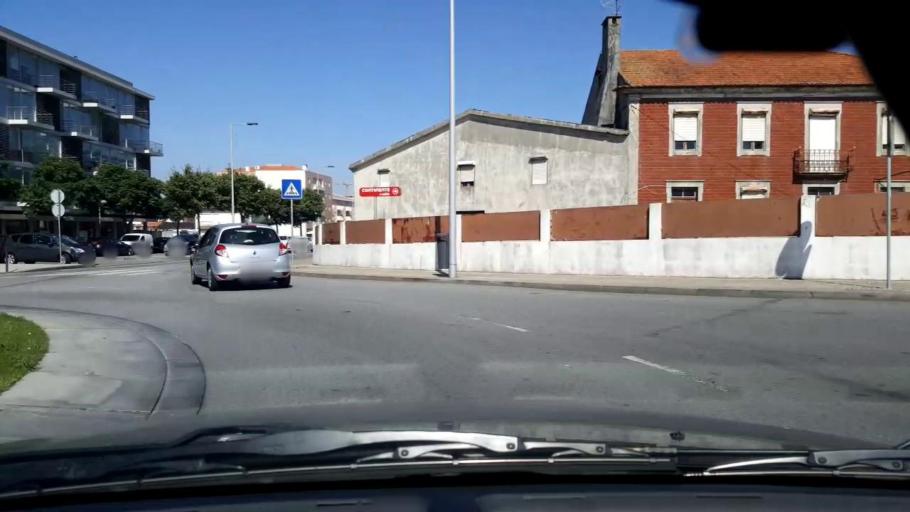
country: PT
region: Porto
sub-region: Vila do Conde
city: Vila do Conde
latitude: 41.3677
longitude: -8.7504
